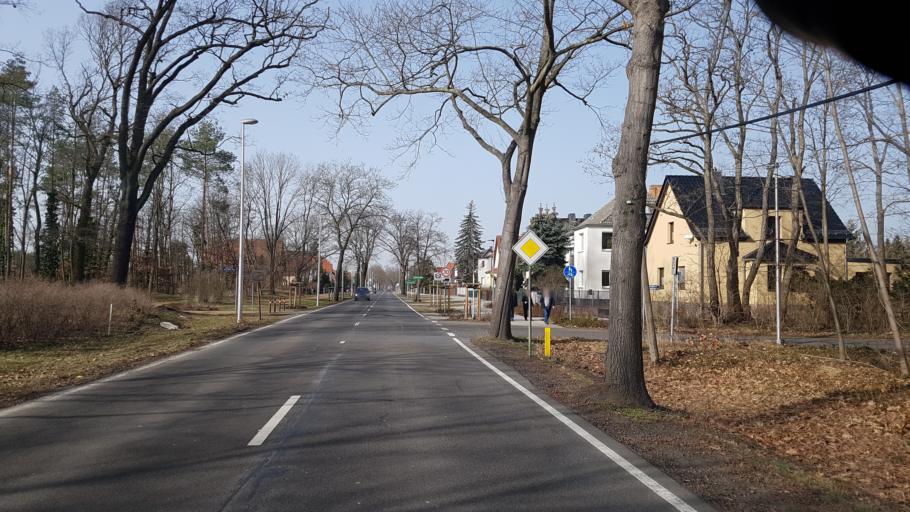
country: DE
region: Brandenburg
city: Cottbus
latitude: 51.7508
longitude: 14.3672
